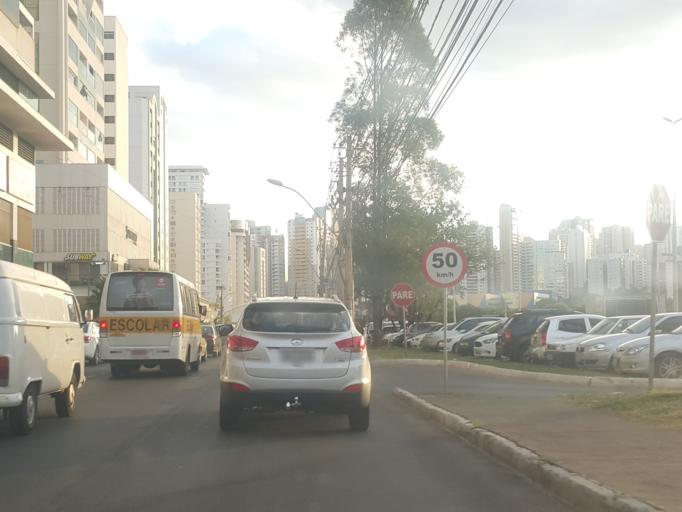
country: BR
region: Federal District
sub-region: Brasilia
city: Brasilia
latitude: -15.8362
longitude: -48.0198
